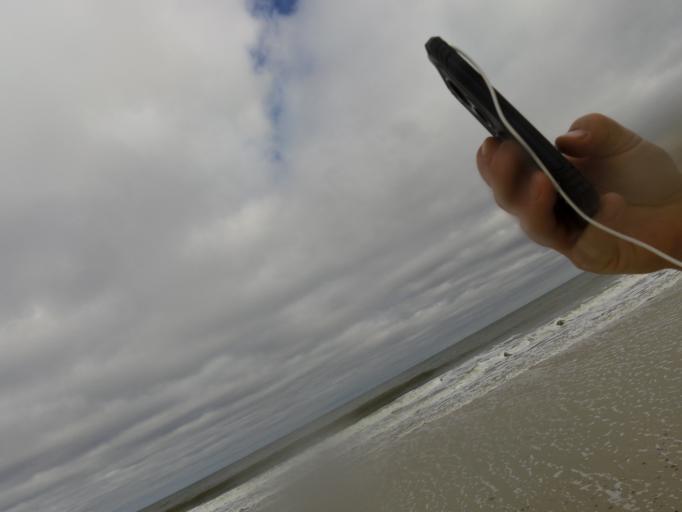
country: US
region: Florida
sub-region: Nassau County
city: Fernandina Beach
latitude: 30.5594
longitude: -81.4423
